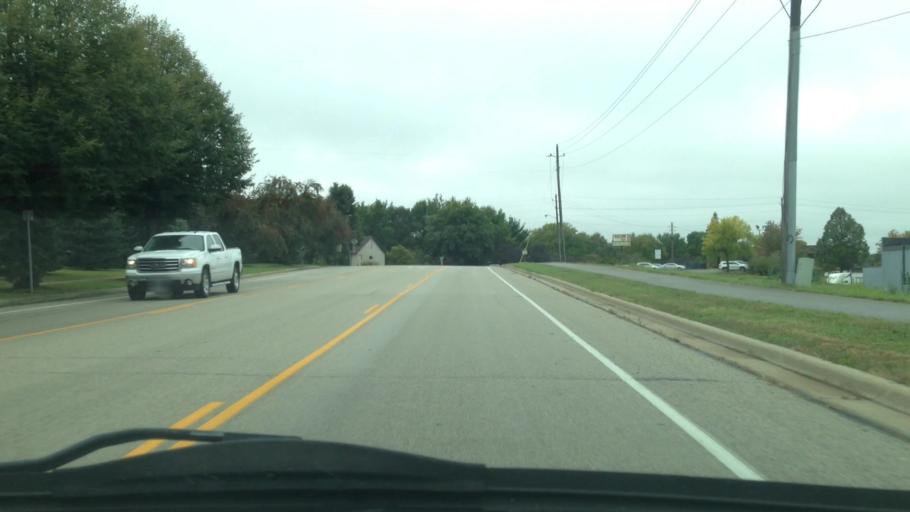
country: US
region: Minnesota
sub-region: Olmsted County
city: Rochester
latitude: 44.0595
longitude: -92.4710
